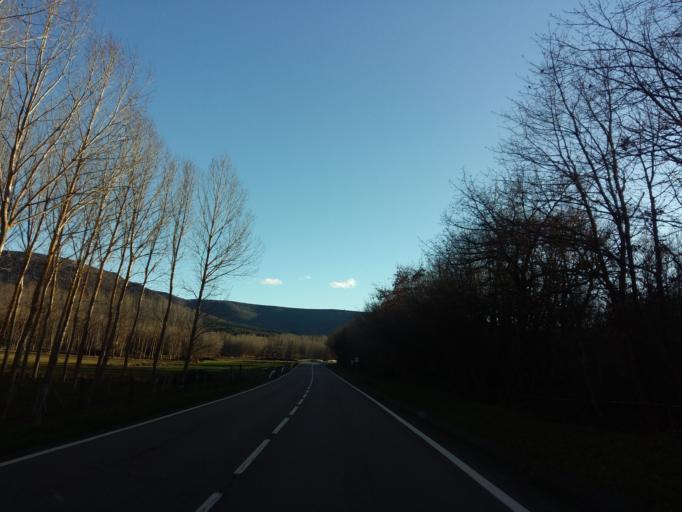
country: ES
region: Cantabria
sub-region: Provincia de Cantabria
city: San Martin de Elines
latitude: 42.8091
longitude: -3.9274
